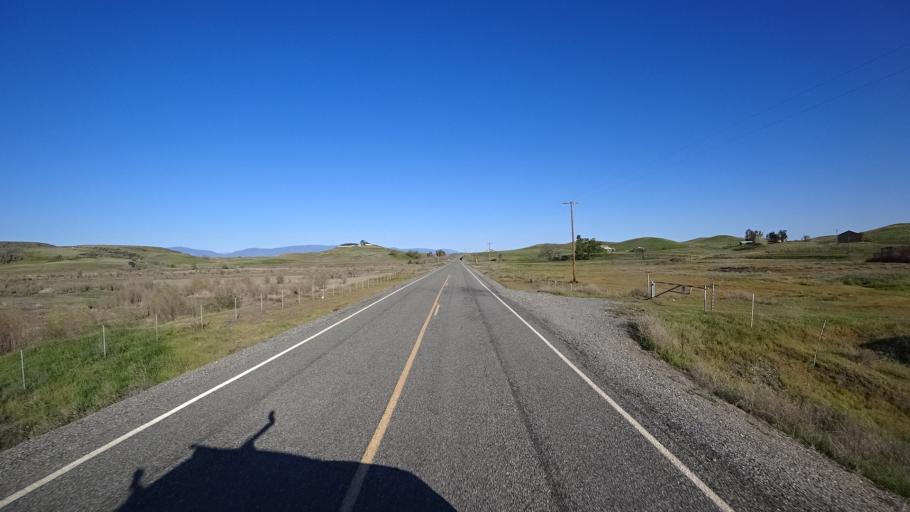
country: US
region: California
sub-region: Glenn County
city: Orland
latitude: 39.8214
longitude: -122.3287
